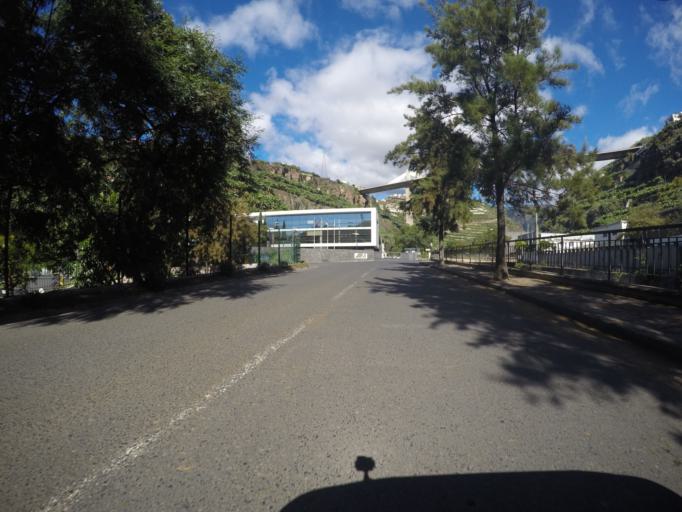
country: PT
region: Madeira
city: Camara de Lobos
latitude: 32.6518
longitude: -16.9647
